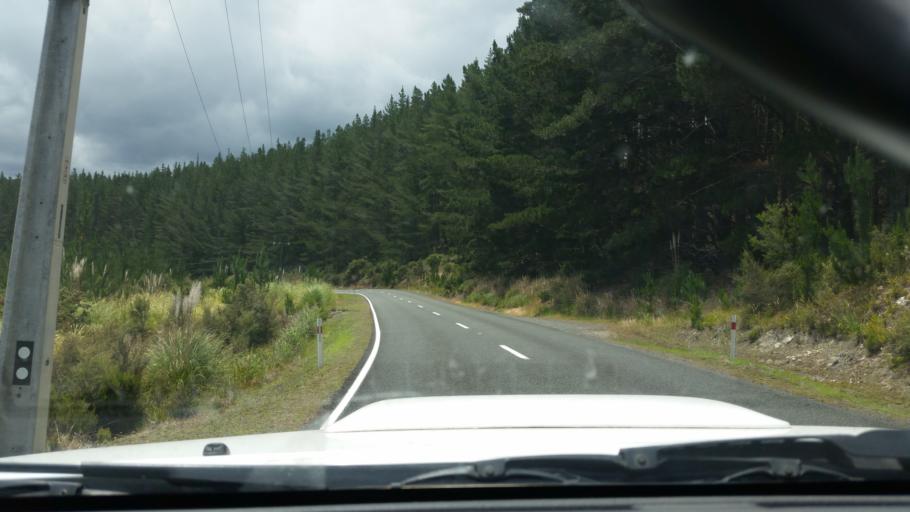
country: NZ
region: Northland
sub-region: Kaipara District
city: Dargaville
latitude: -35.8224
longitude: 173.7079
